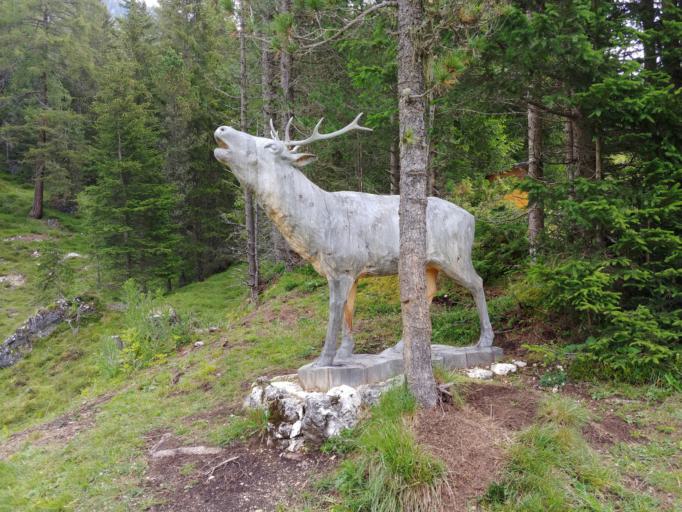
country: IT
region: Trentino-Alto Adige
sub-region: Bolzano
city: Selva
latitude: 46.5654
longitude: 11.7523
